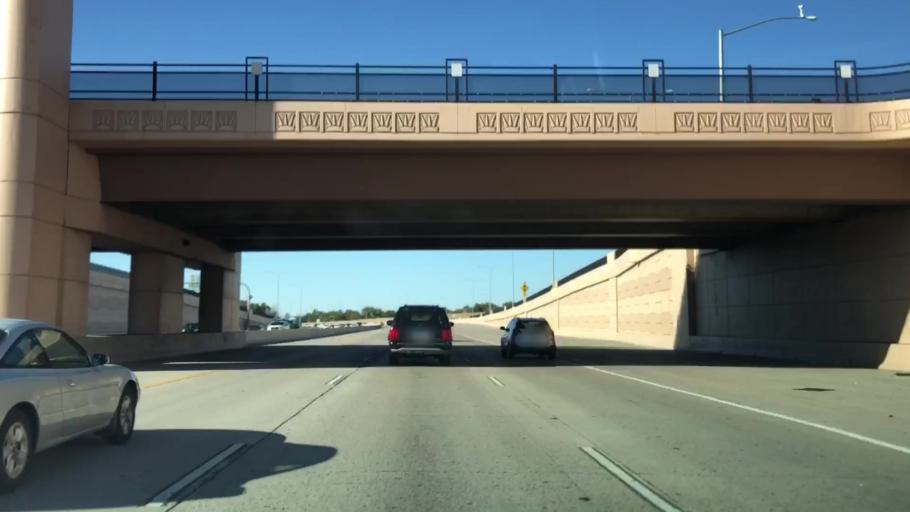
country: US
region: Colorado
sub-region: Adams County
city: Aurora
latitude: 39.7444
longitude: -104.8248
